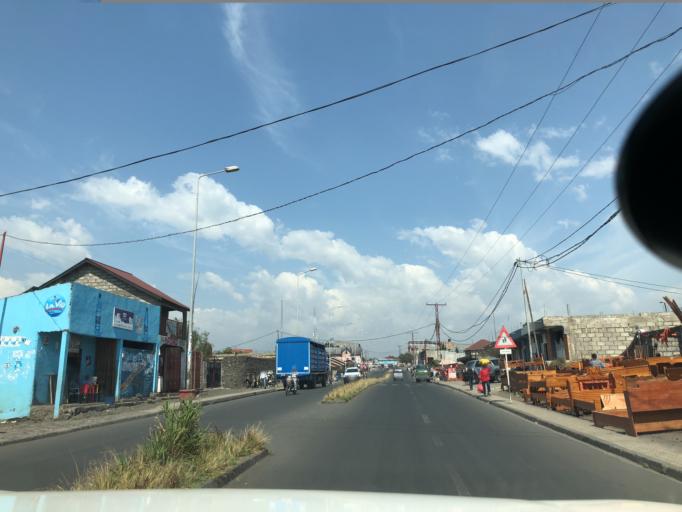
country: CD
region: Nord Kivu
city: Goma
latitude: -1.6573
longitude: 29.1943
